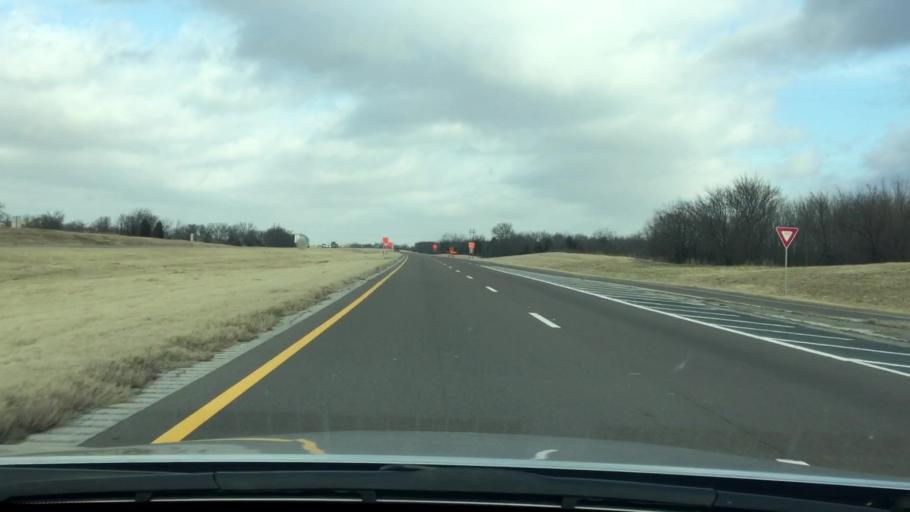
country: US
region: Oklahoma
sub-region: Garvin County
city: Maysville
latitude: 34.8292
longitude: -97.3101
